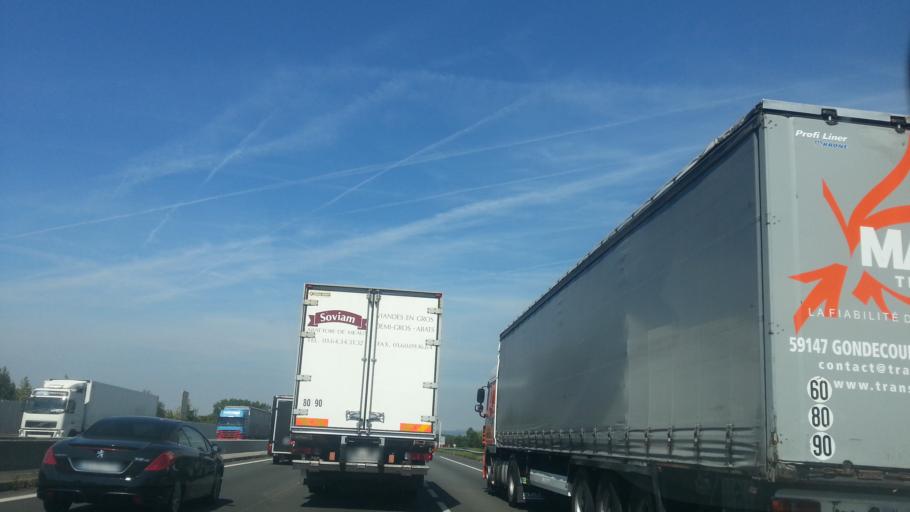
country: FR
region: Ile-de-France
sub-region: Departement du Val-d'Oise
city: Survilliers
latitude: 49.1003
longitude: 2.5505
